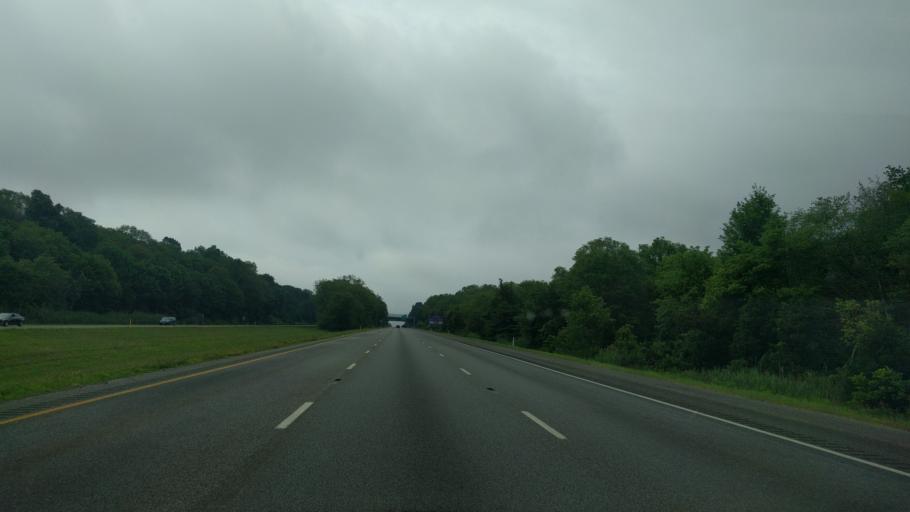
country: US
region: Massachusetts
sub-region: Bristol County
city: Ocean Grove
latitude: 41.7589
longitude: -71.2286
